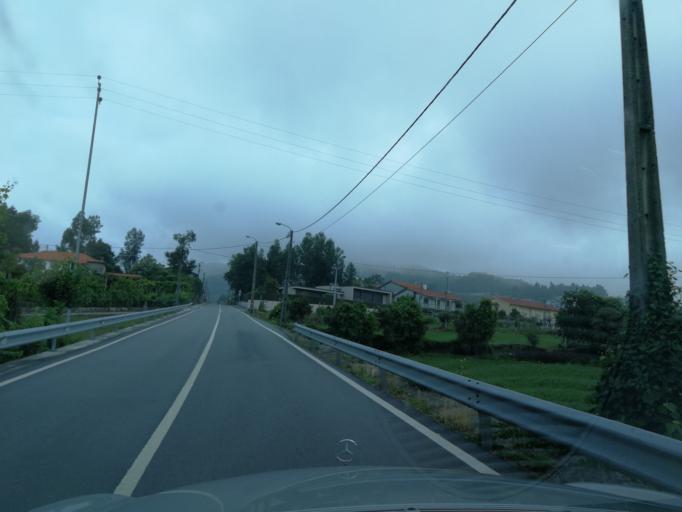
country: PT
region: Braga
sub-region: Guimaraes
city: Ponte
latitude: 41.5104
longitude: -8.3540
